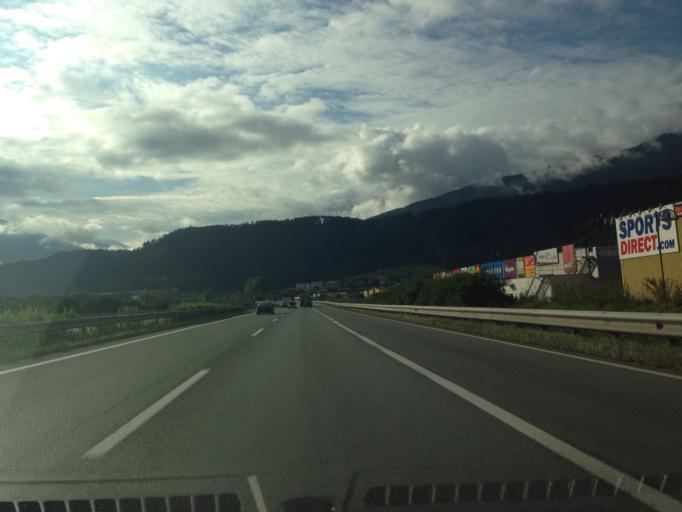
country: AT
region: Tyrol
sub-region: Politischer Bezirk Innsbruck Land
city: Vols
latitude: 47.2603
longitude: 11.3230
